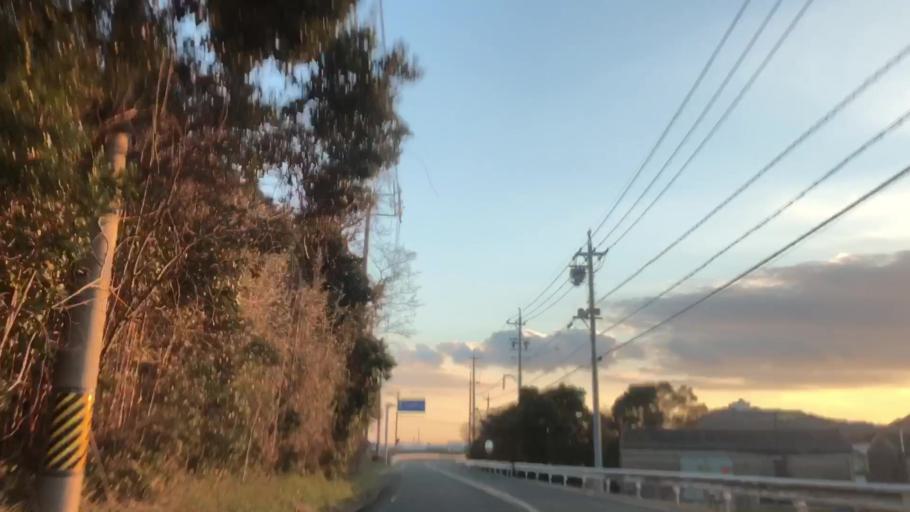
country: JP
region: Aichi
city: Toyohama
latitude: 34.5960
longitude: 137.0485
